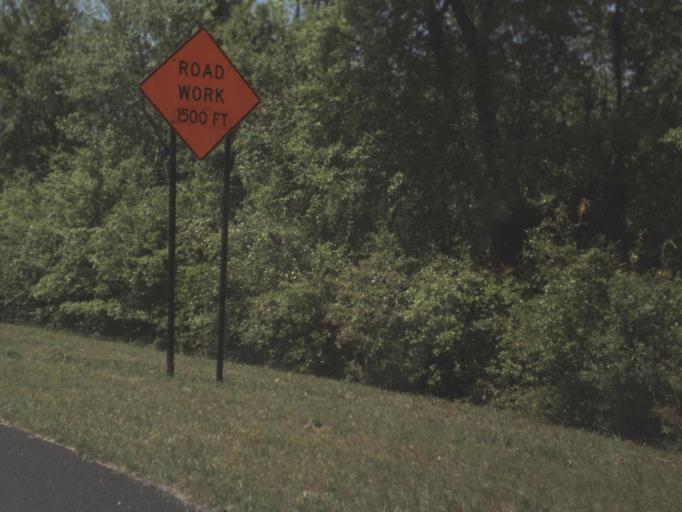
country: US
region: Florida
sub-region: Santa Rosa County
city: Pace
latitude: 30.5881
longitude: -87.1769
